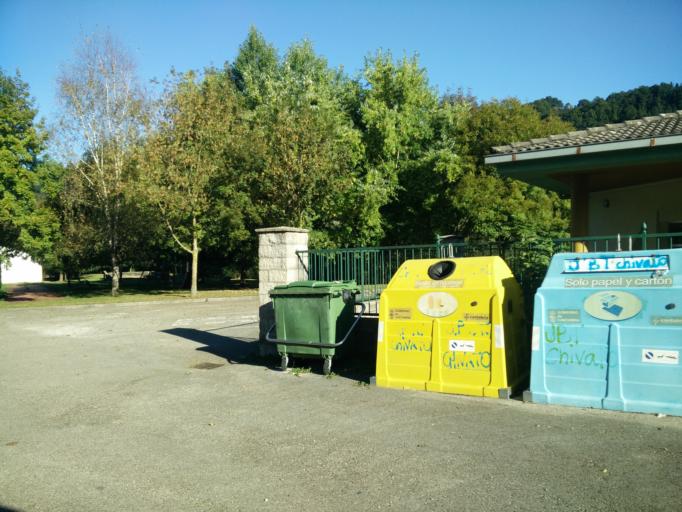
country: ES
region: Cantabria
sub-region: Provincia de Cantabria
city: Vega de Pas
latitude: 43.1578
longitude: -3.7868
